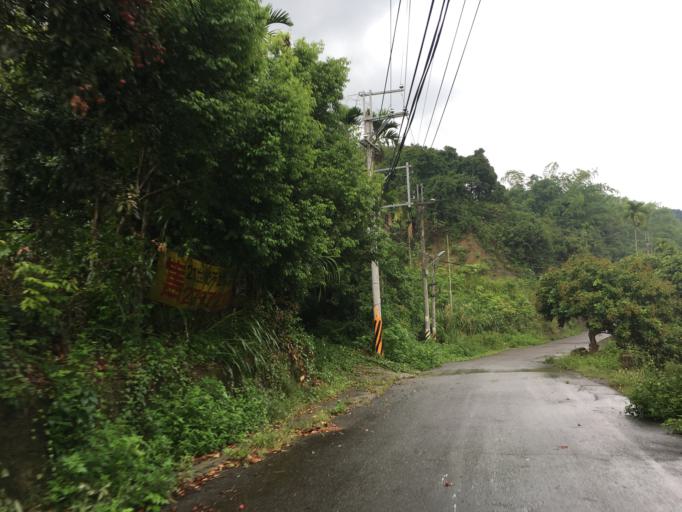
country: TW
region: Taiwan
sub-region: Taichung City
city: Taichung
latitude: 24.0601
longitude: 120.7479
